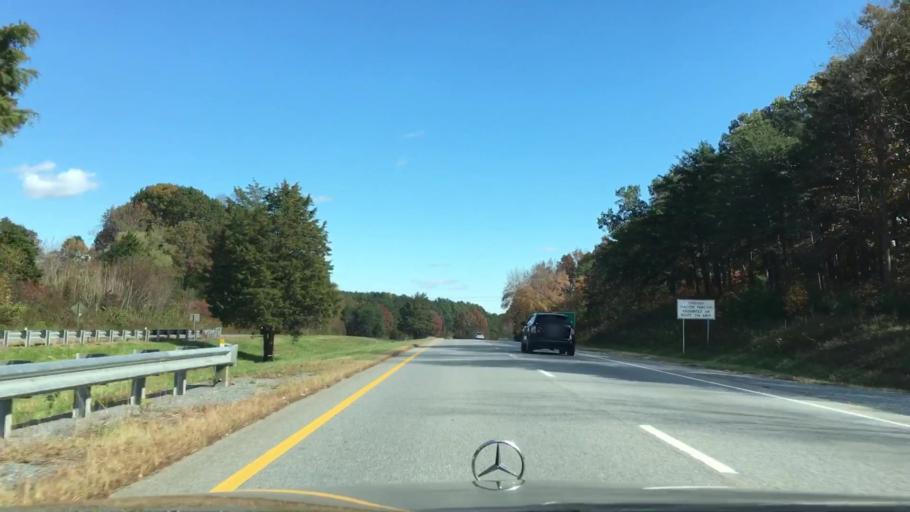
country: US
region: Virginia
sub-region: Campbell County
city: Altavista
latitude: 37.1330
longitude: -79.2966
